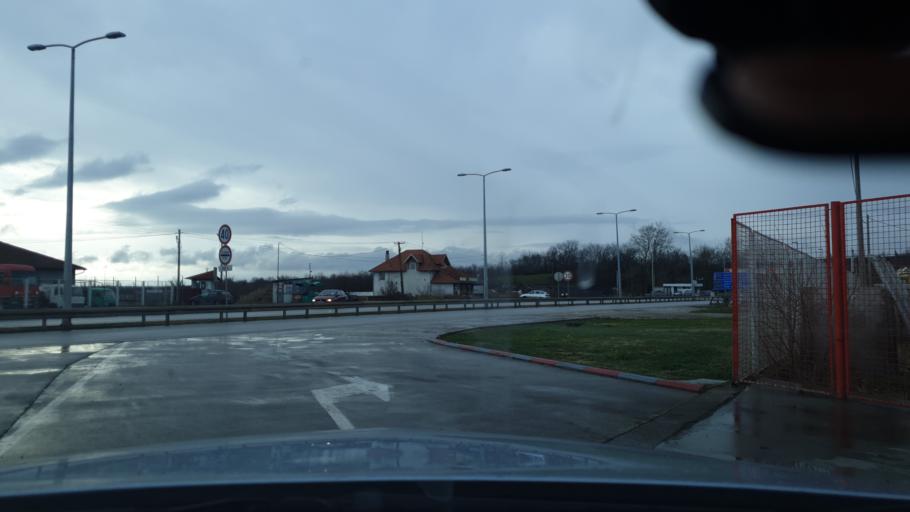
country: RS
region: Central Serbia
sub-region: Podunavski Okrug
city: Smederevo
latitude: 44.5812
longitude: 20.9842
